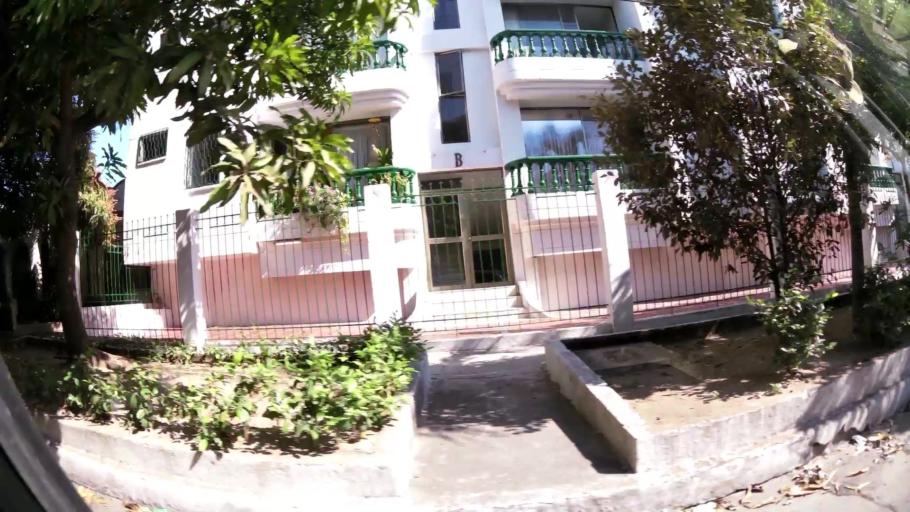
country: CO
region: Atlantico
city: Barranquilla
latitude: 10.9921
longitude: -74.7969
